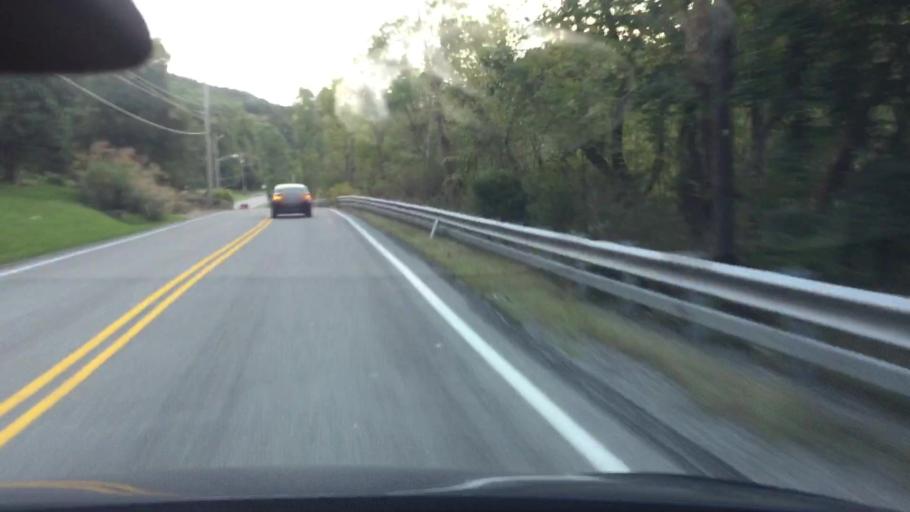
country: US
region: Pennsylvania
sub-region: Allegheny County
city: Allison Park
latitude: 40.5413
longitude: -79.9193
